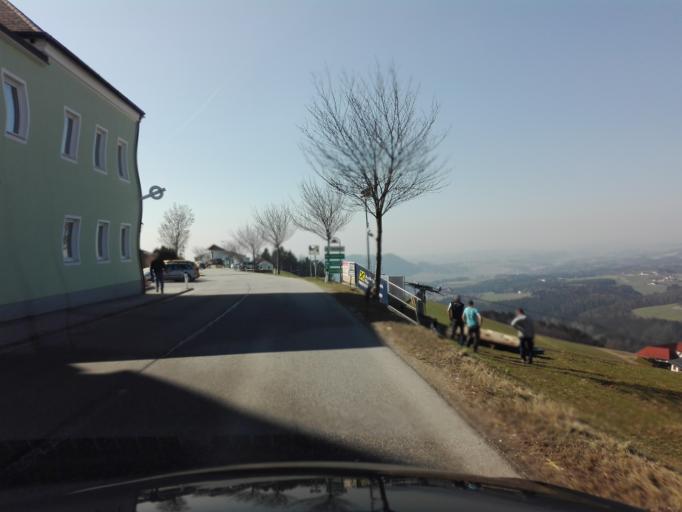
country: AT
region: Upper Austria
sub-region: Politischer Bezirk Perg
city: Perg
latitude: 48.3020
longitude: 14.6517
